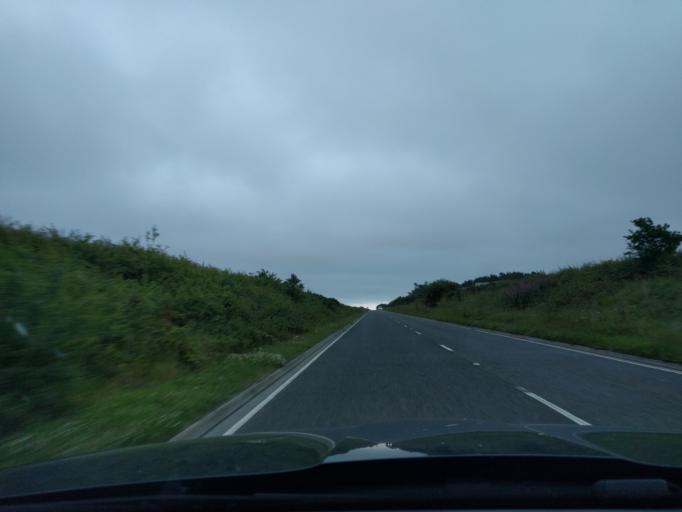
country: GB
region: England
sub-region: Northumberland
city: Felton
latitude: 55.2502
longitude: -1.6968
